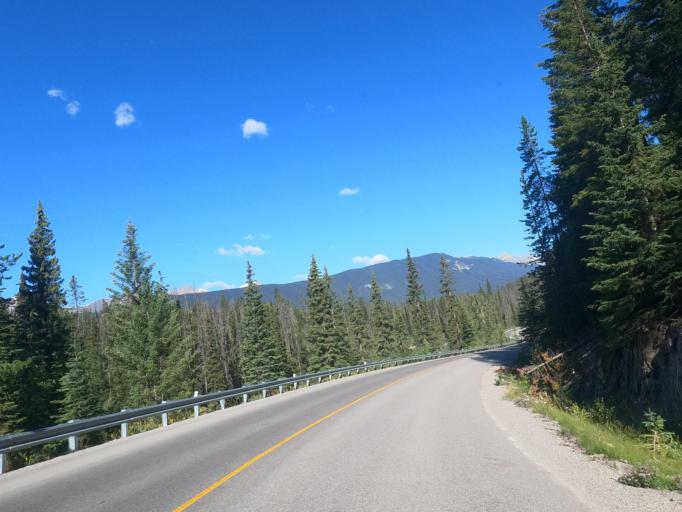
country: CA
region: Alberta
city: Lake Louise
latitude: 51.3807
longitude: -116.5232
